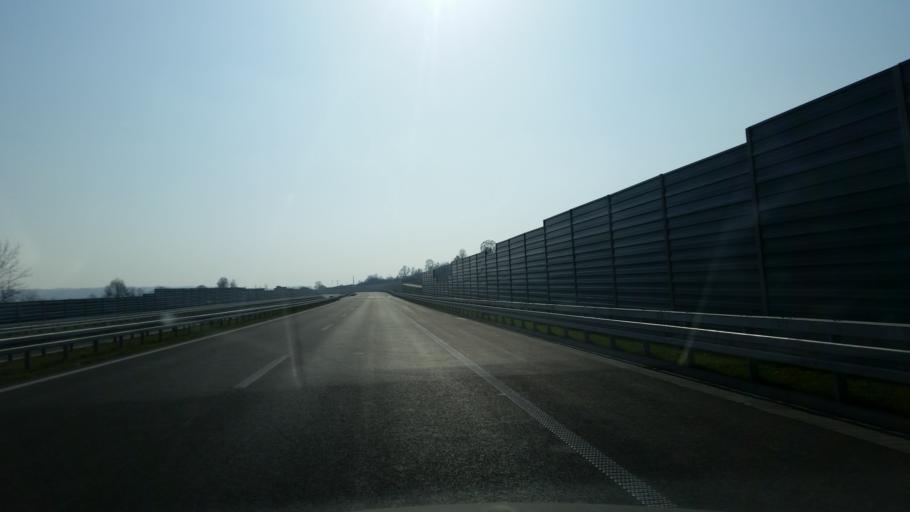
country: RS
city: Prislonica
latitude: 43.9653
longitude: 20.3960
